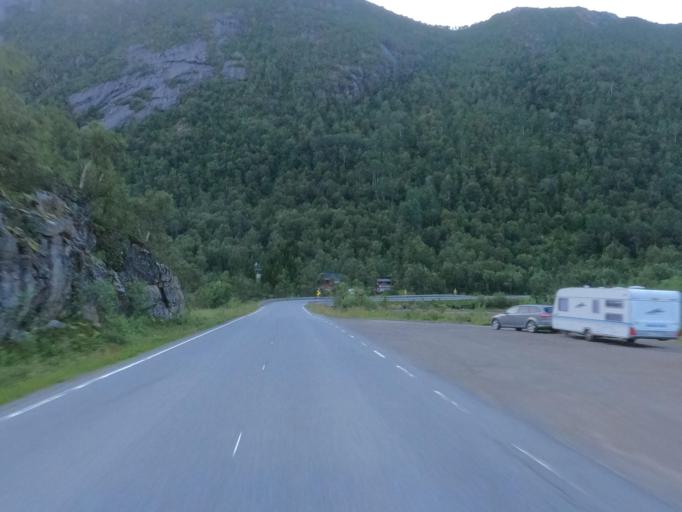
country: NO
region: Nordland
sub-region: Lodingen
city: Lodingen
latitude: 68.5596
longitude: 15.7509
